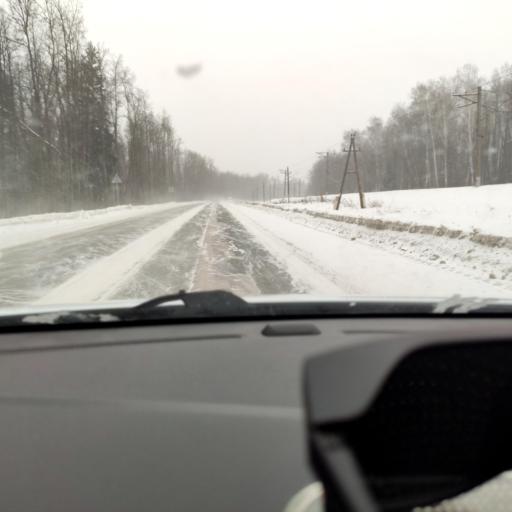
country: RU
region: Tatarstan
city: Vysokaya Gora
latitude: 55.9177
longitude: 49.2813
